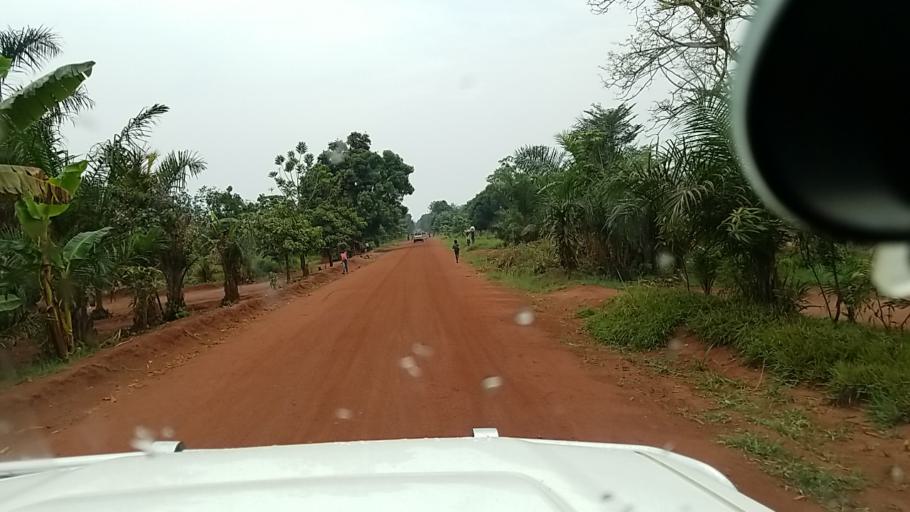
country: CD
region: Equateur
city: Gemena
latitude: 3.2186
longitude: 19.7820
